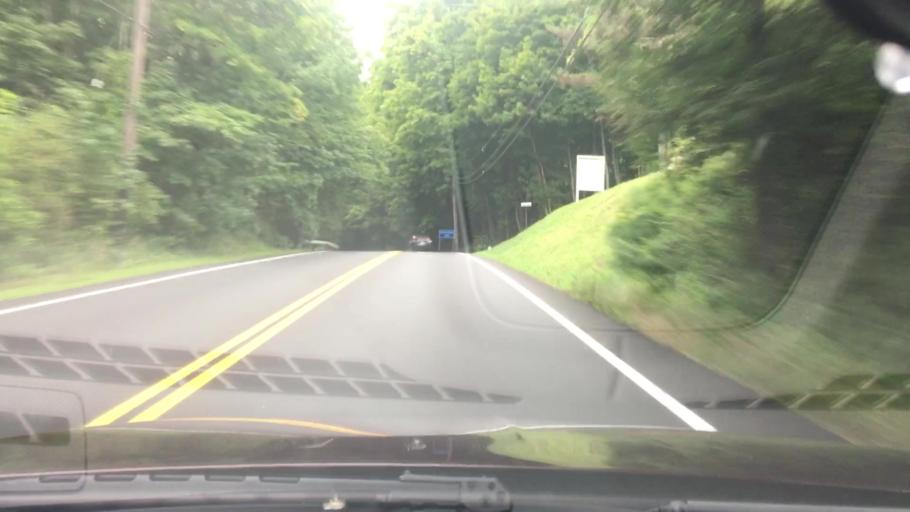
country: US
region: New York
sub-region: Dutchess County
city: Dover Plains
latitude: 41.8452
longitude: -73.5659
